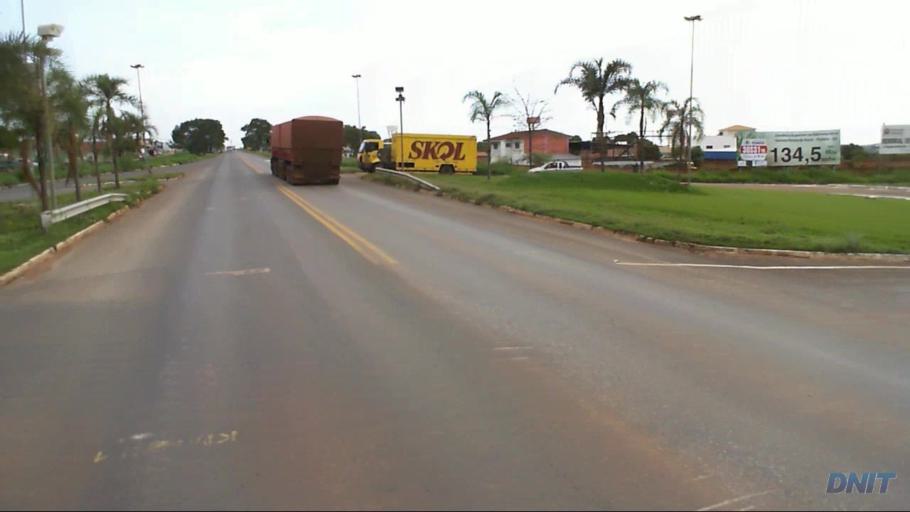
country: BR
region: Goias
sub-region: Uruacu
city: Uruacu
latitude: -14.5332
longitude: -49.1609
